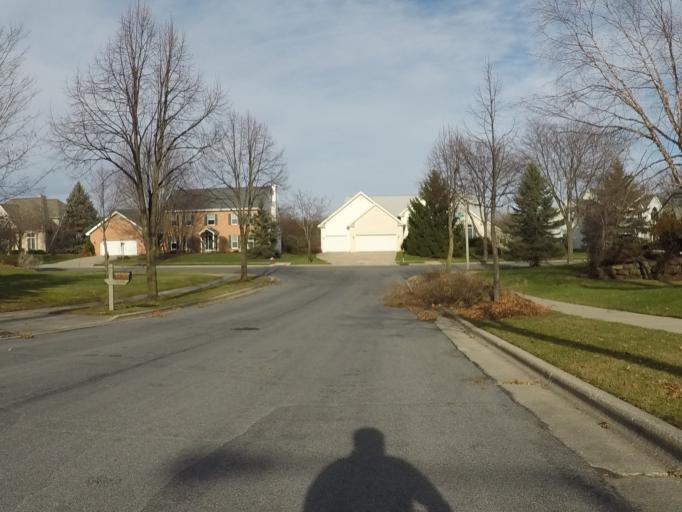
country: US
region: Wisconsin
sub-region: Dane County
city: Middleton
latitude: 43.0766
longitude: -89.5397
